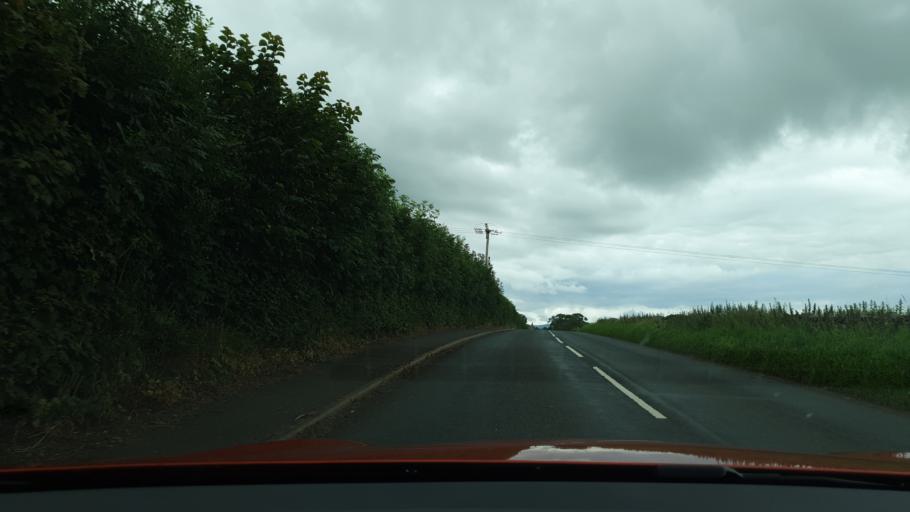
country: GB
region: England
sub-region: Cumbria
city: Penrith
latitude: 54.6378
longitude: -2.7623
